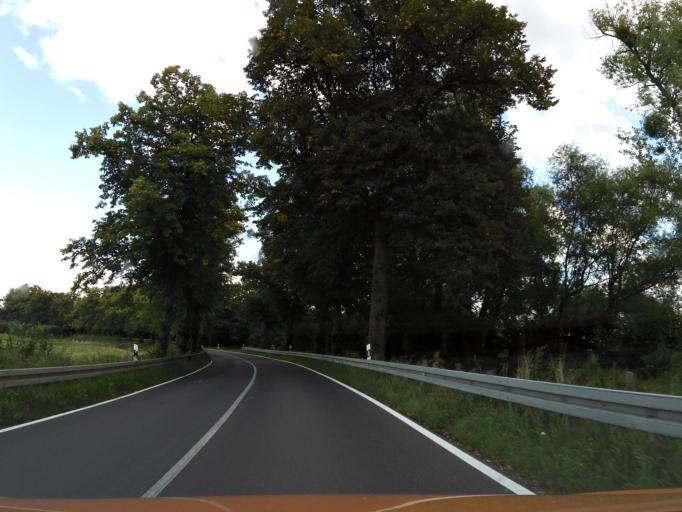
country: DE
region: Brandenburg
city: Potsdam
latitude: 52.4610
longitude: 13.0056
